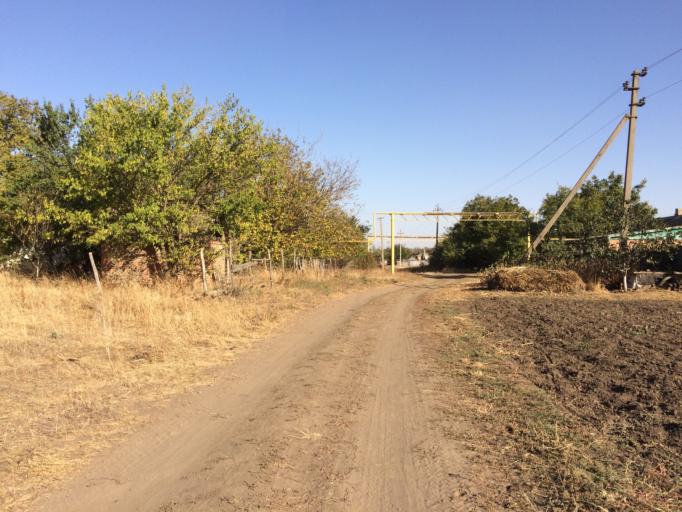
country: RU
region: Rostov
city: Tselina
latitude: 46.5247
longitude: 41.1828
